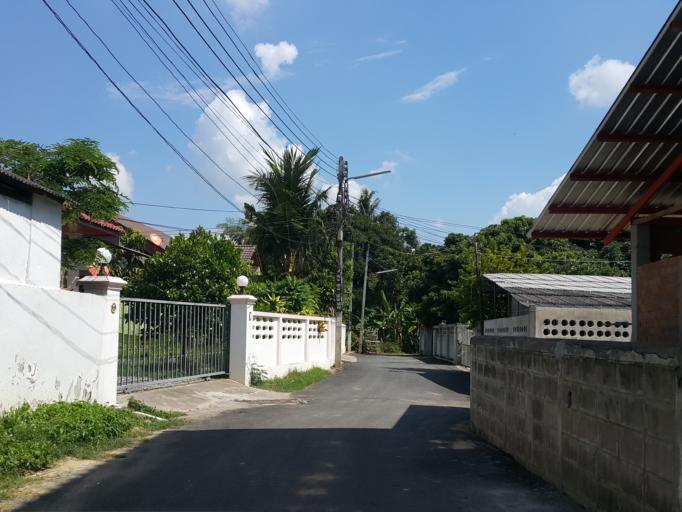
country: TH
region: Chiang Mai
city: Saraphi
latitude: 18.7642
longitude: 99.0554
